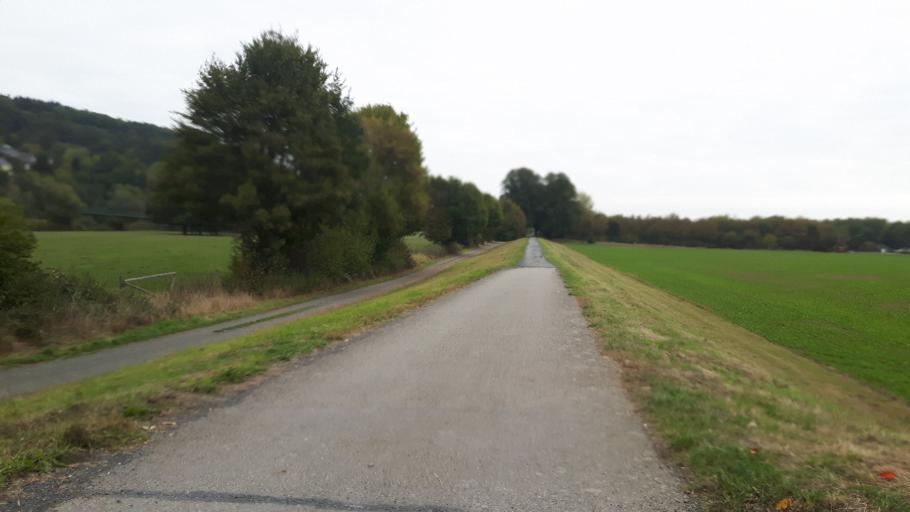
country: DE
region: North Rhine-Westphalia
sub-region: Regierungsbezirk Koln
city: Hennef
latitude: 50.7883
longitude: 7.2785
